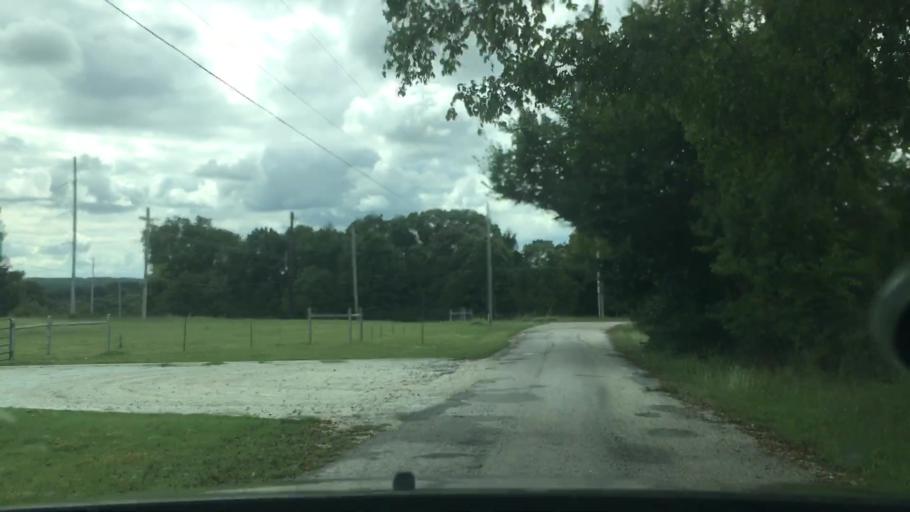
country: US
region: Oklahoma
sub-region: Pontotoc County
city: Ada
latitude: 34.7526
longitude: -96.6515
